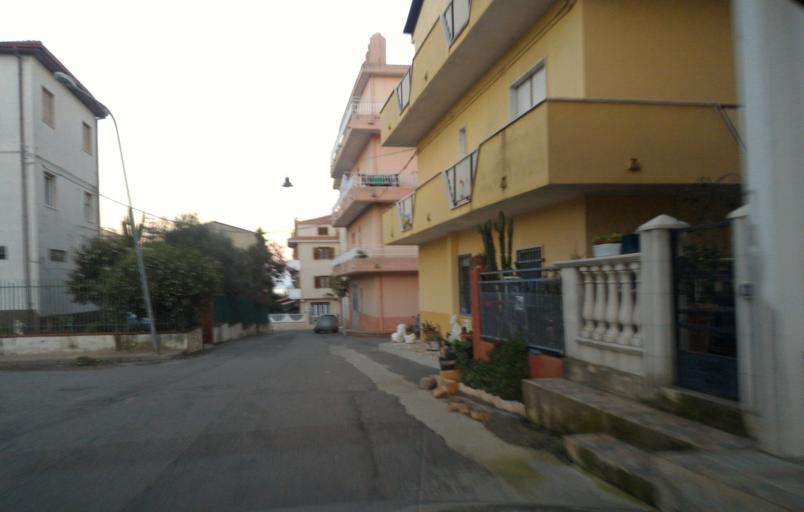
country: IT
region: Calabria
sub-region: Provincia di Crotone
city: Torretta
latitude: 39.4534
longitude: 17.0350
